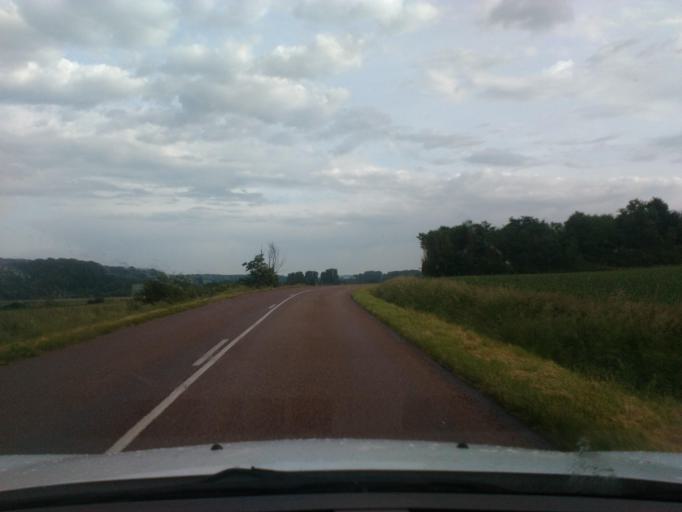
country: FR
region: Lorraine
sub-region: Departement des Vosges
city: Rambervillers
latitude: 48.3964
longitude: 6.5920
